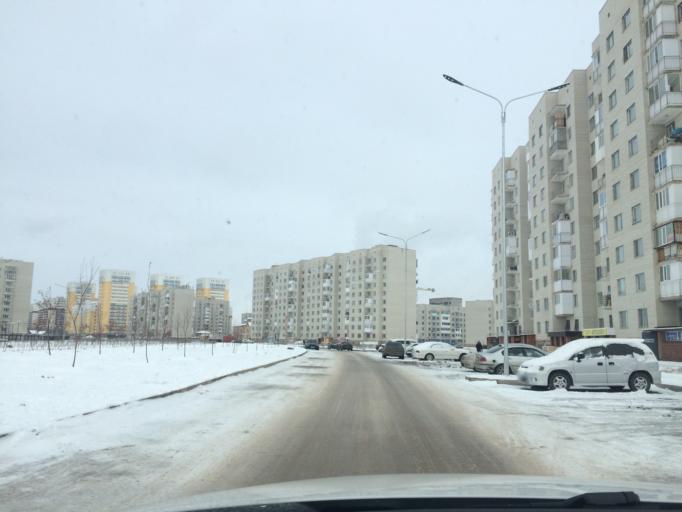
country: KZ
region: Astana Qalasy
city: Astana
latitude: 51.1237
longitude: 71.5050
